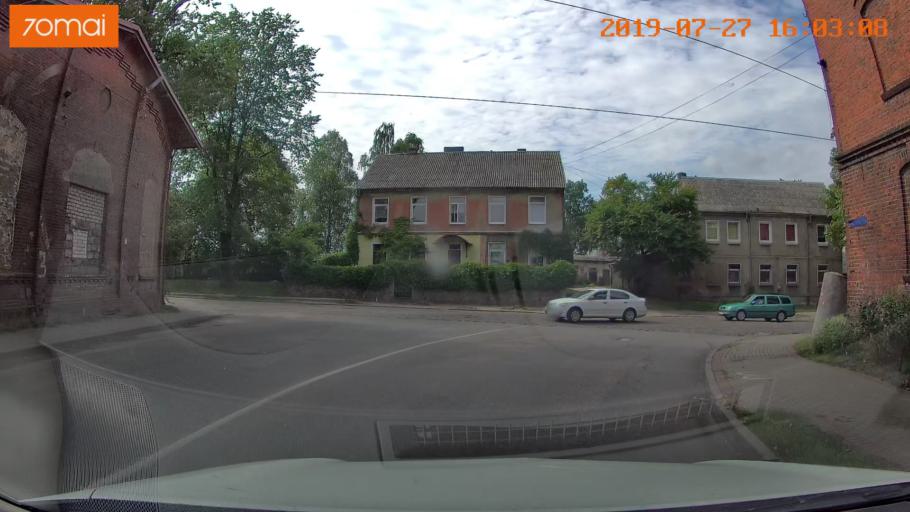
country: RU
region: Kaliningrad
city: Chernyakhovsk
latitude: 54.6313
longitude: 21.8030
